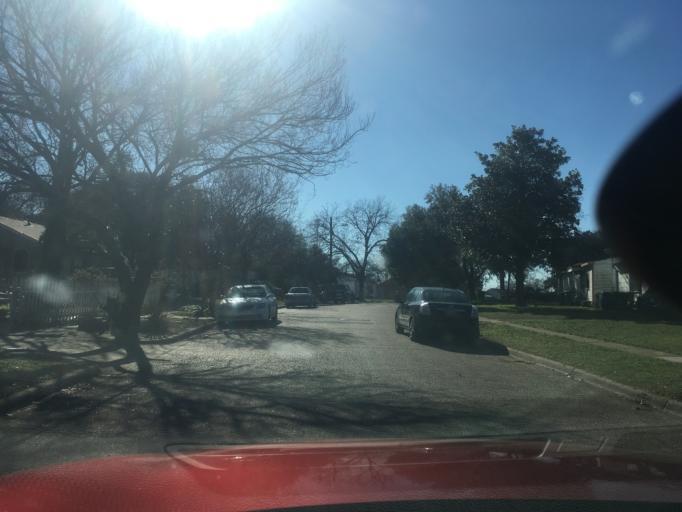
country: US
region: Texas
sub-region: Dallas County
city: Cockrell Hill
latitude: 32.7065
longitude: -96.8324
